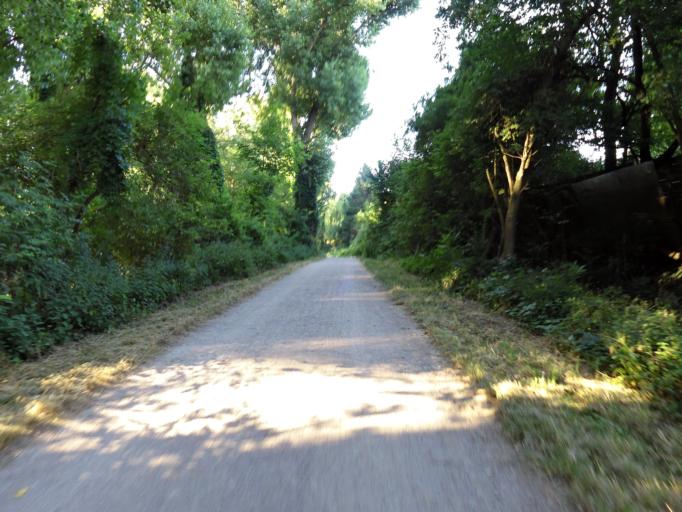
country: DE
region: Rheinland-Pfalz
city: Mutterstadt
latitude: 49.4730
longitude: 8.3651
